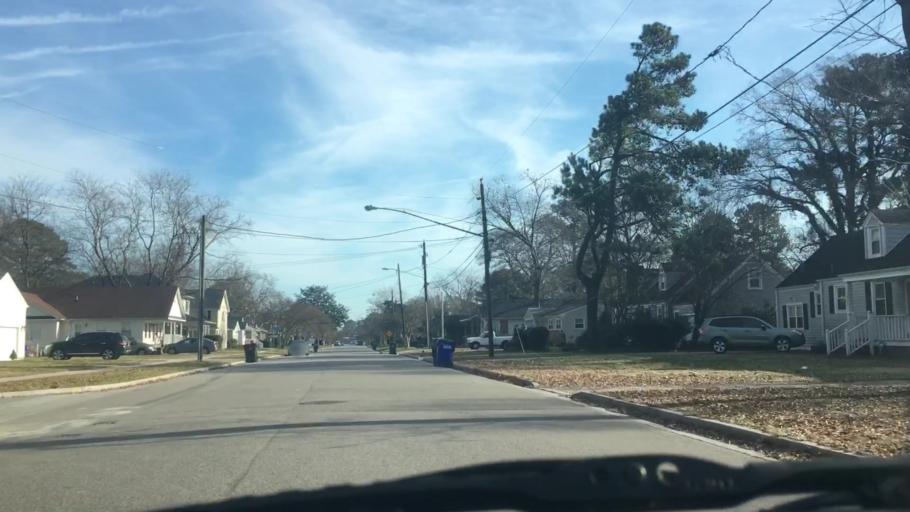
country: US
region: Virginia
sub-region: City of Norfolk
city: Norfolk
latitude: 36.8670
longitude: -76.2563
